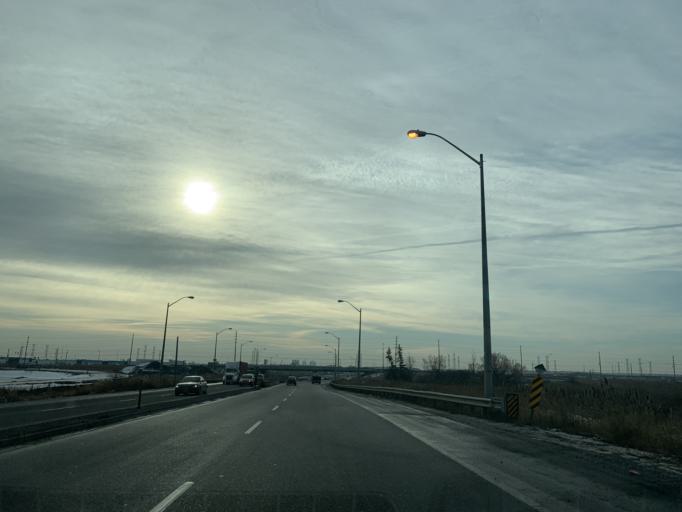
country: CA
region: Ontario
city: Etobicoke
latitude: 43.7733
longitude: -79.6352
